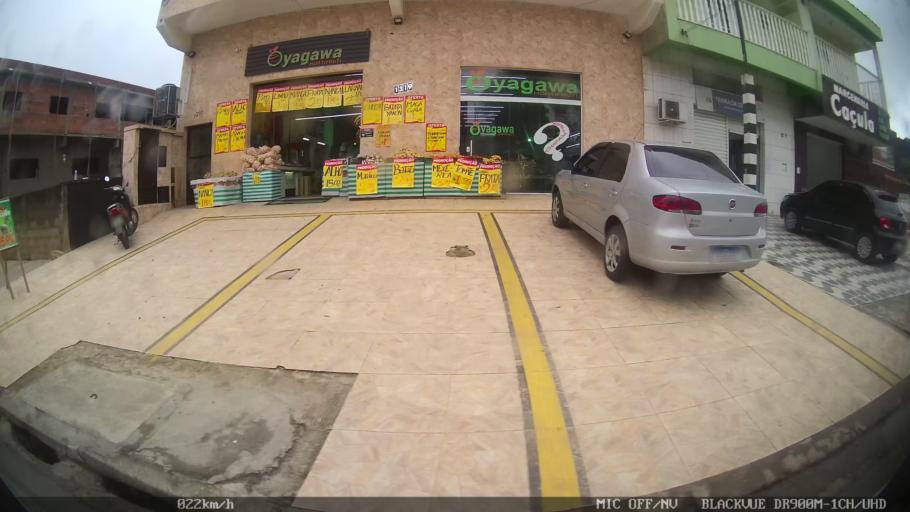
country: BR
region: Sao Paulo
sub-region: Juquia
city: Juquia
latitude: -24.3154
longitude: -47.6316
